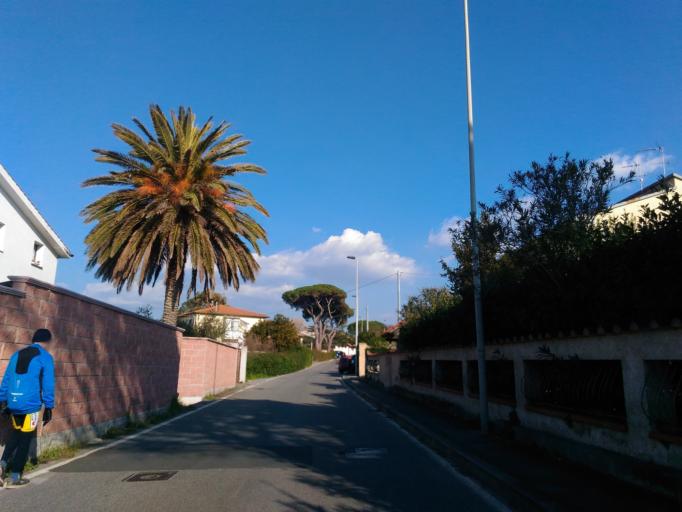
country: IT
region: Tuscany
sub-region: Provincia di Livorno
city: Livorno
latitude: 43.5115
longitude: 10.3348
